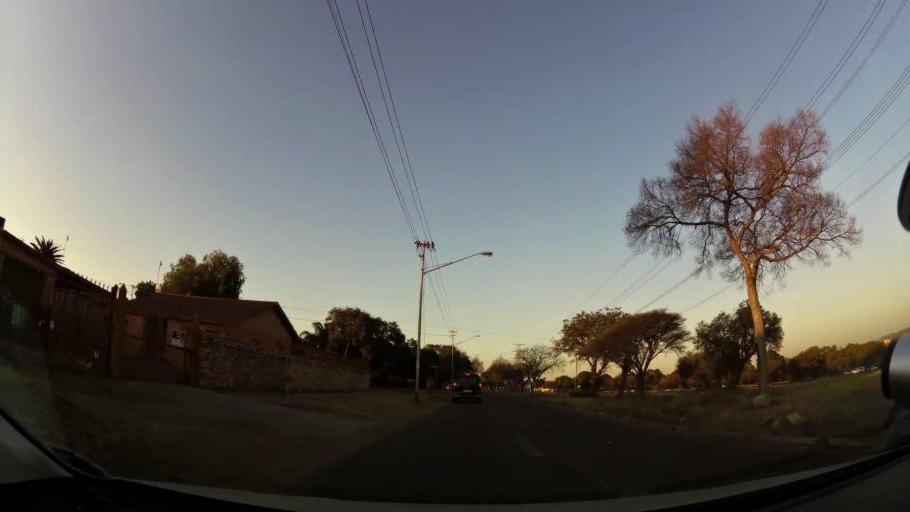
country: ZA
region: Gauteng
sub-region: City of Tshwane Metropolitan Municipality
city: Pretoria
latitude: -25.7447
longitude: 28.1322
